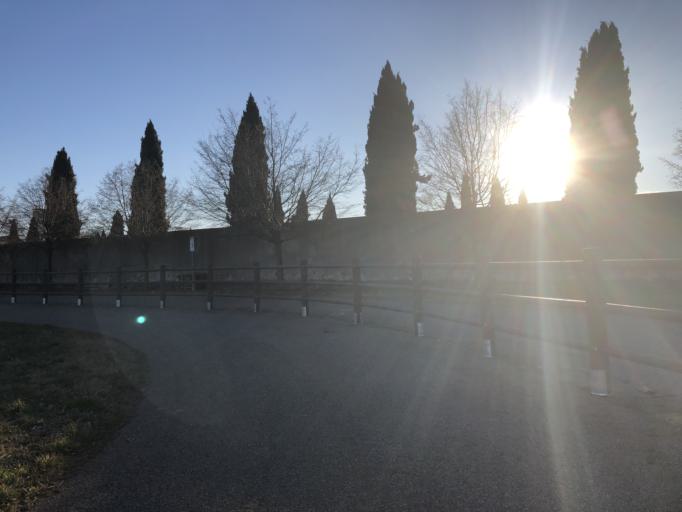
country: IT
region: Veneto
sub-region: Provincia di Verona
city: Caselle
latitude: 45.4194
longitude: 10.9002
